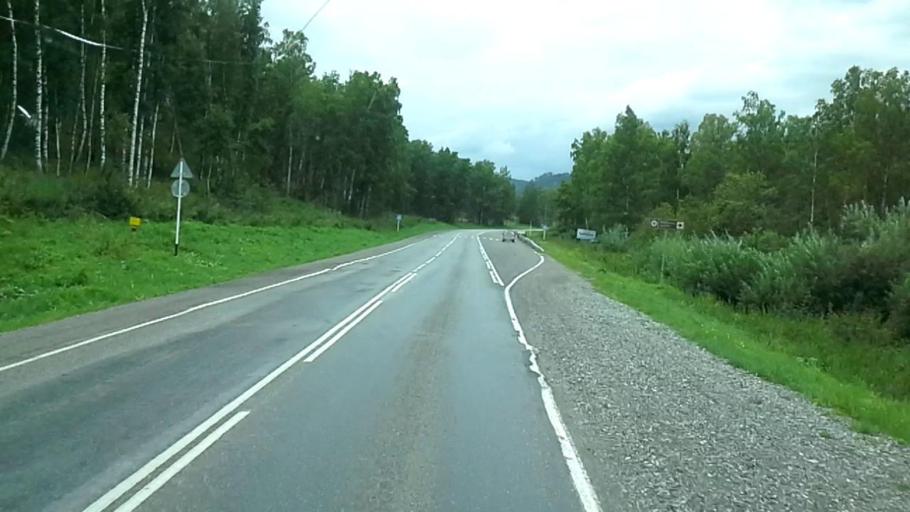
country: RU
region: Altay
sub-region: Mayminskiy Rayon
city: Manzherok
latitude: 51.8576
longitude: 85.7550
